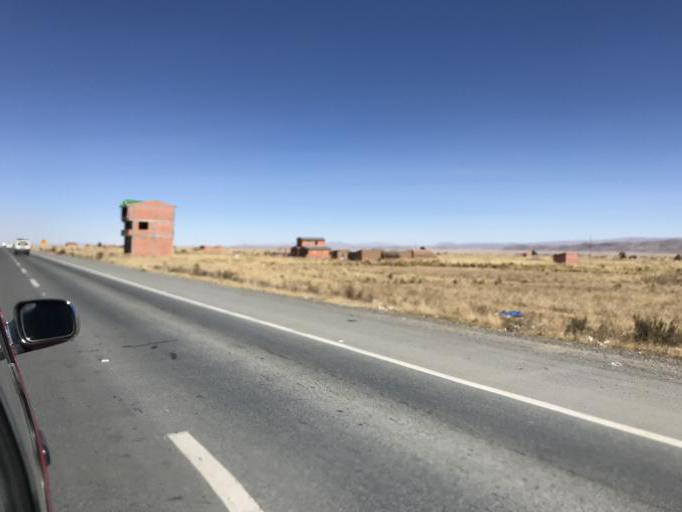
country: BO
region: La Paz
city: Batallas
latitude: -16.3544
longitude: -68.3999
